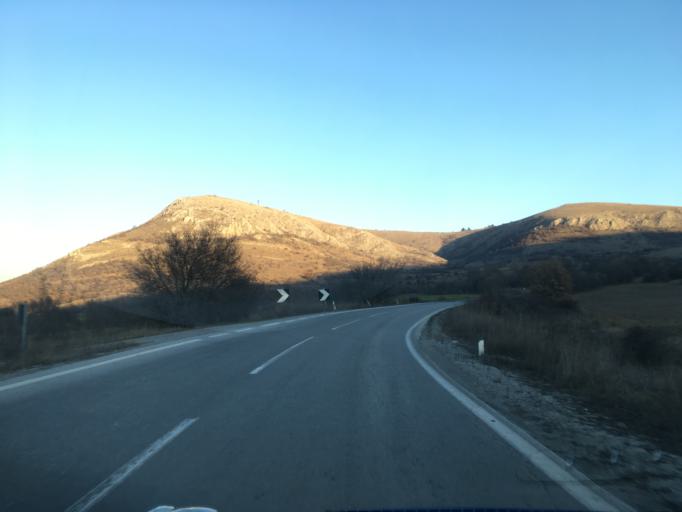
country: GR
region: West Macedonia
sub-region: Nomos Kozanis
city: Kozani
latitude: 40.3164
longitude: 21.7561
